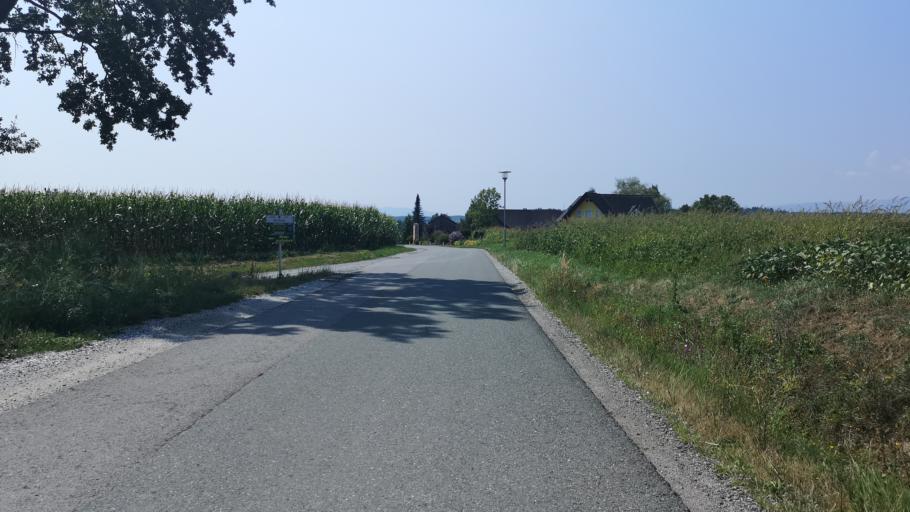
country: AT
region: Styria
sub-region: Politischer Bezirk Deutschlandsberg
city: Preding
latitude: 46.8604
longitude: 15.3891
